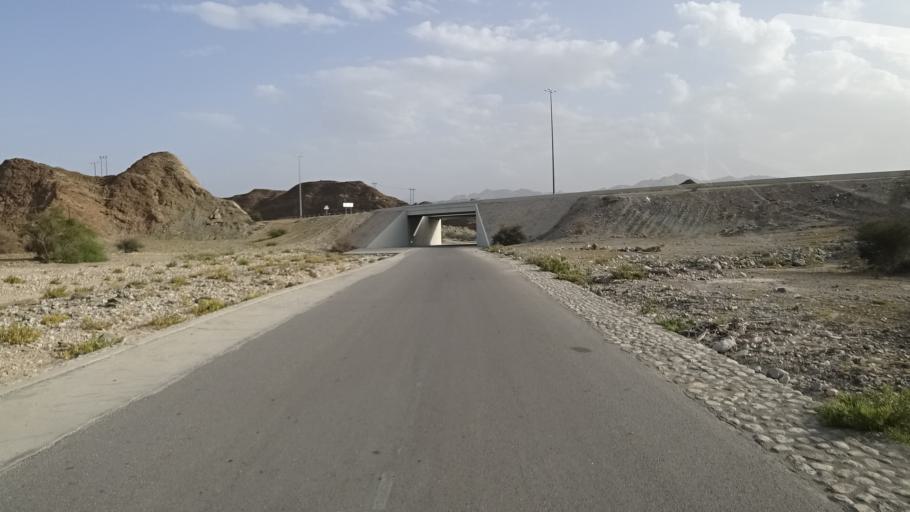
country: OM
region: Muhafazat Masqat
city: Bawshar
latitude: 23.3535
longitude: 58.5353
